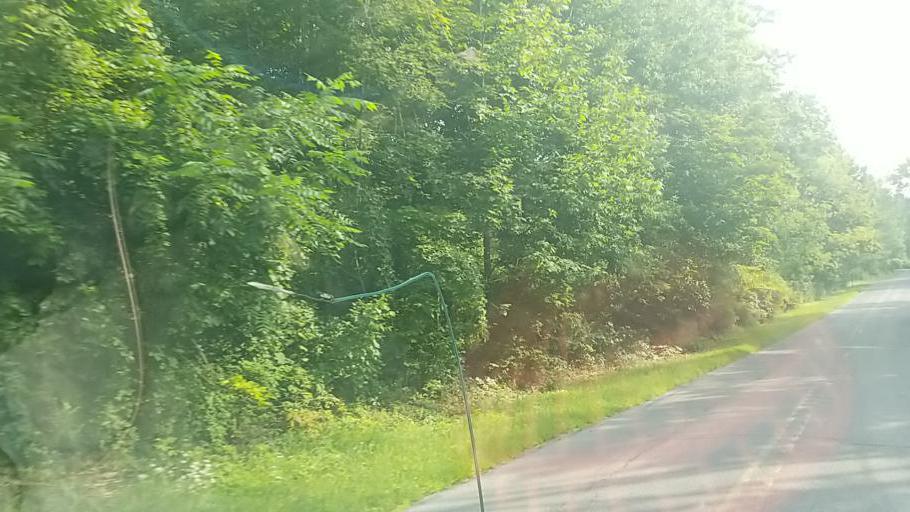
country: US
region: New York
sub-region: Fulton County
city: Broadalbin
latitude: 43.0747
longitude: -74.2271
